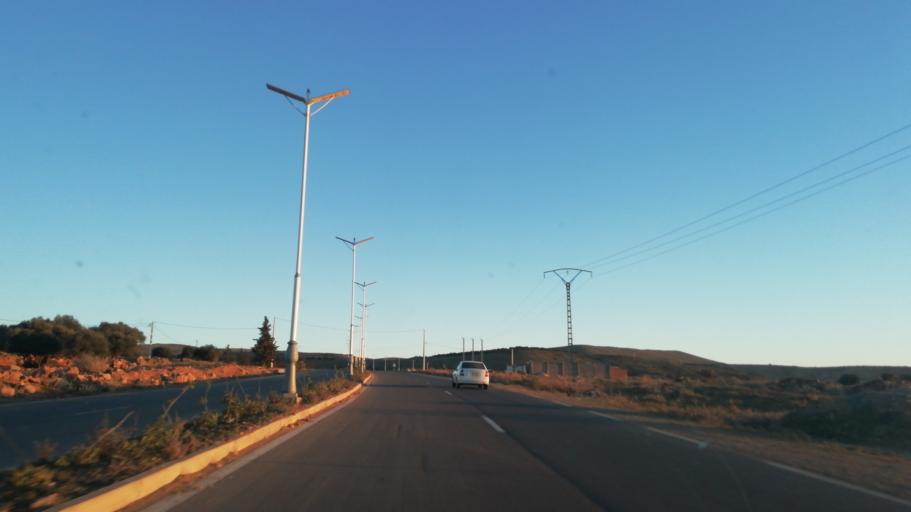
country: DZ
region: Saida
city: Saida
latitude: 34.8604
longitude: 0.1954
